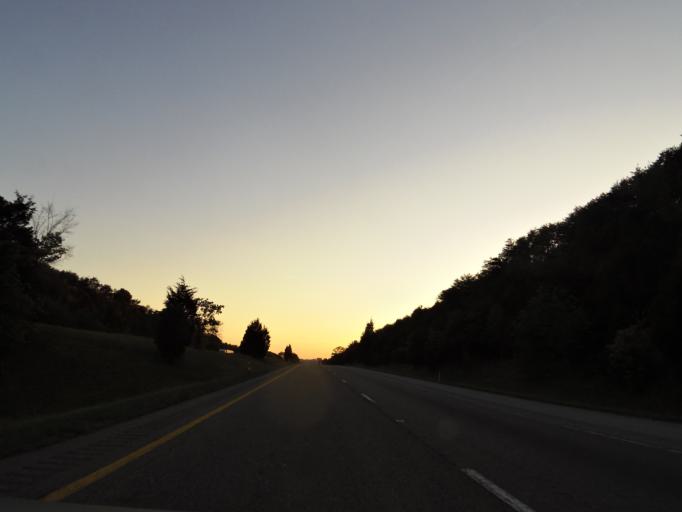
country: US
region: Tennessee
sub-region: Greene County
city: Mosheim
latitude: 36.2008
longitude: -83.1260
